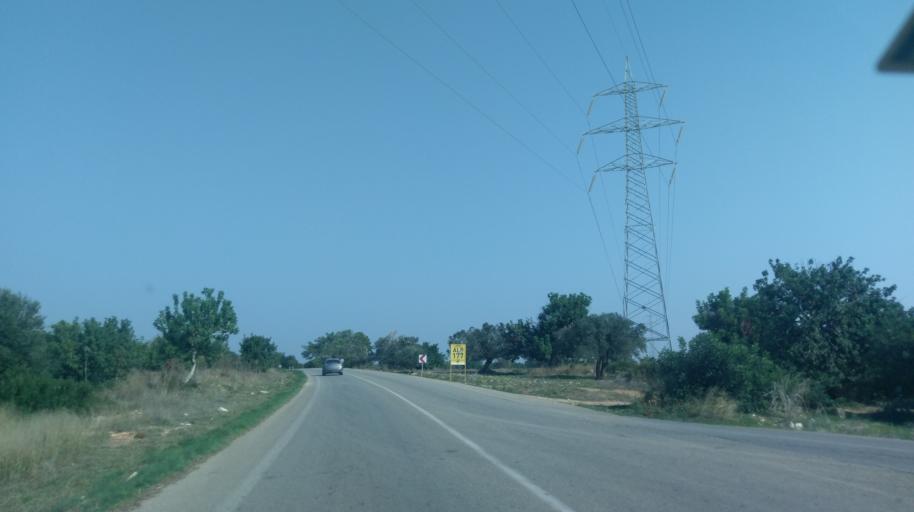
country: CY
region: Ammochostos
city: Leonarisso
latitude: 35.4819
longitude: 34.1462
